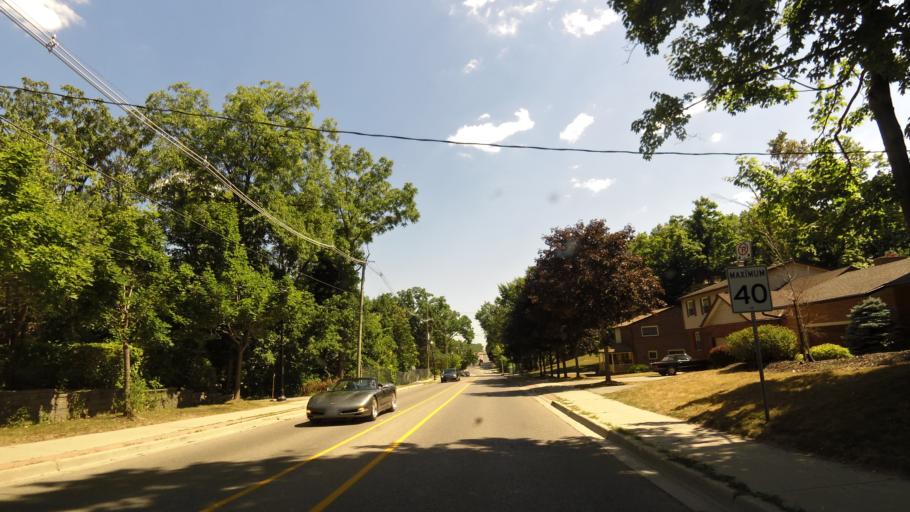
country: CA
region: Ontario
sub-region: Halton
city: Milton
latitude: 43.6478
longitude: -79.9240
